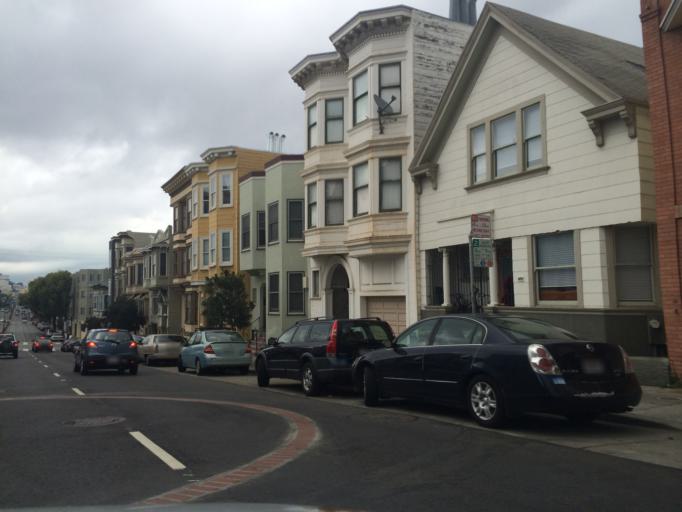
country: US
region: California
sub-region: San Francisco County
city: San Francisco
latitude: 37.7591
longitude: -122.4235
